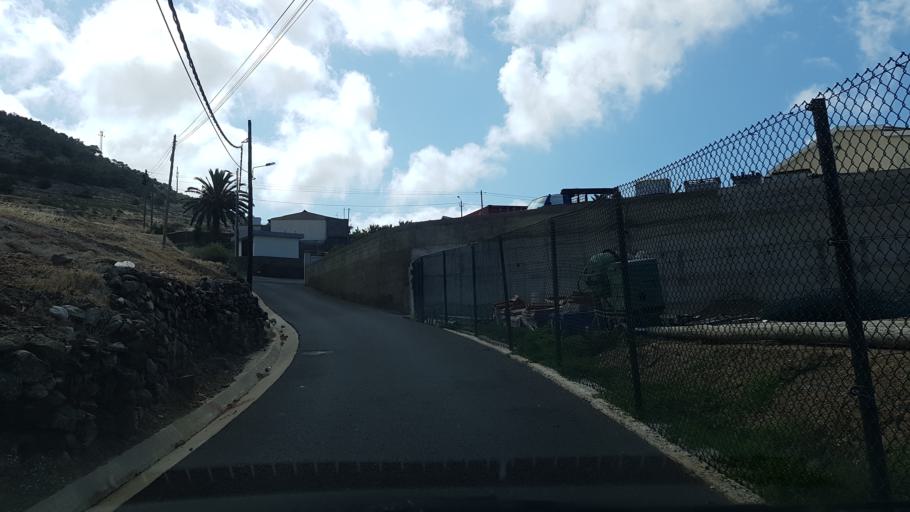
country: PT
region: Madeira
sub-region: Porto Santo
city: Vila de Porto Santo
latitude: 33.0719
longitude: -16.3268
